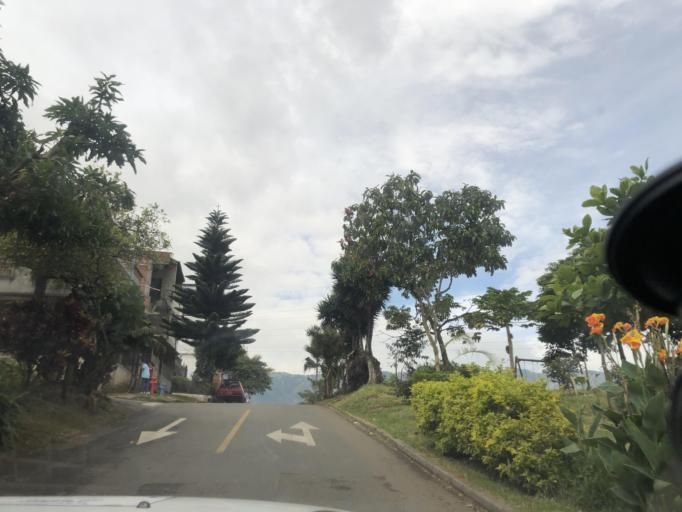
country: CO
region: Antioquia
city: Bello
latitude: 6.3320
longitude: -75.5435
